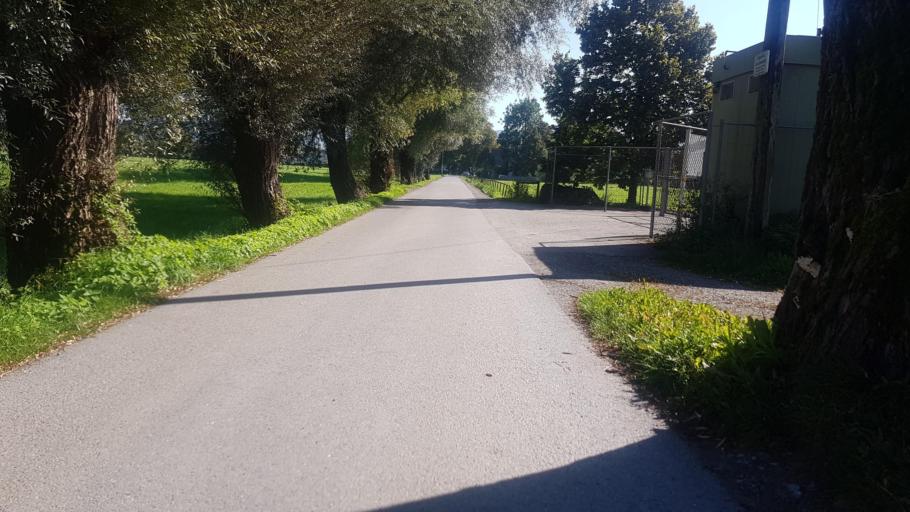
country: AT
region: Vorarlberg
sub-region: Politischer Bezirk Bregenz
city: Fussach
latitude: 47.4825
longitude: 9.6605
